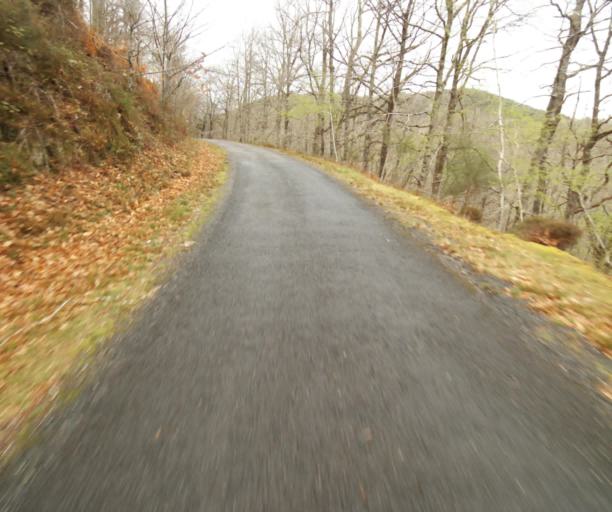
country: FR
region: Limousin
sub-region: Departement de la Correze
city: Saint-Privat
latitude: 45.2110
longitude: 2.0354
